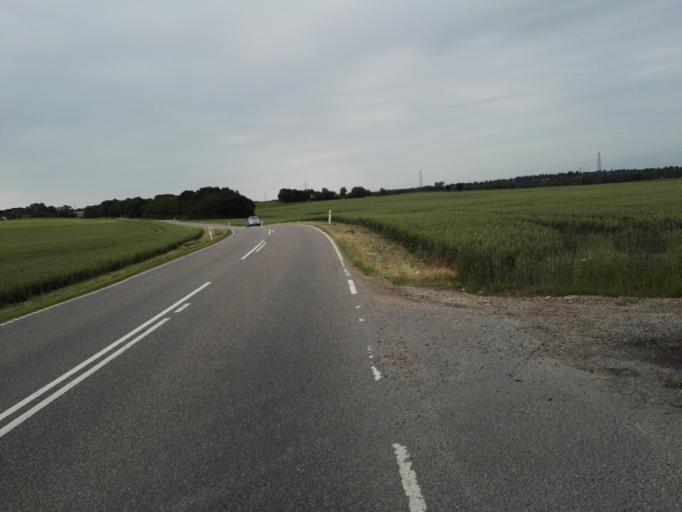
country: DK
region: Zealand
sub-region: Roskilde Kommune
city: Jyllinge
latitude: 55.7825
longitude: 12.1184
